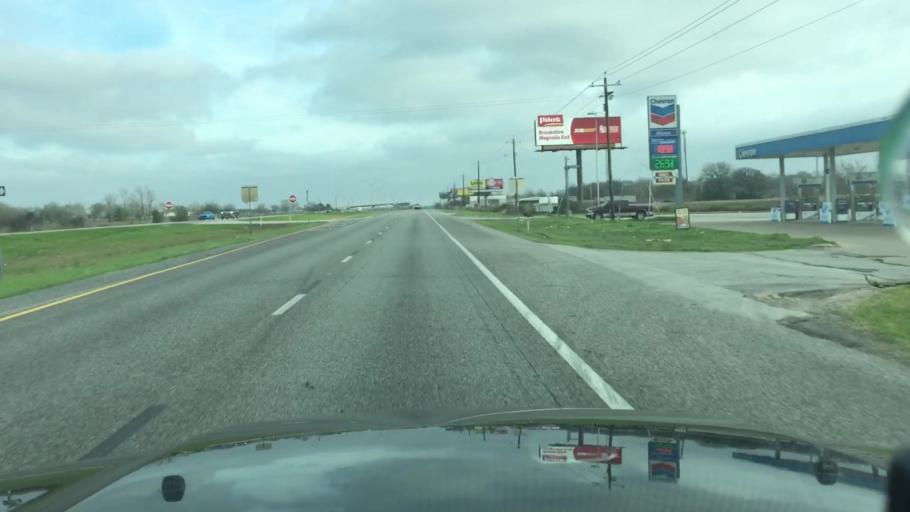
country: US
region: Texas
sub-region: Waller County
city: Hempstead
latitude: 30.1179
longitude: -96.0912
